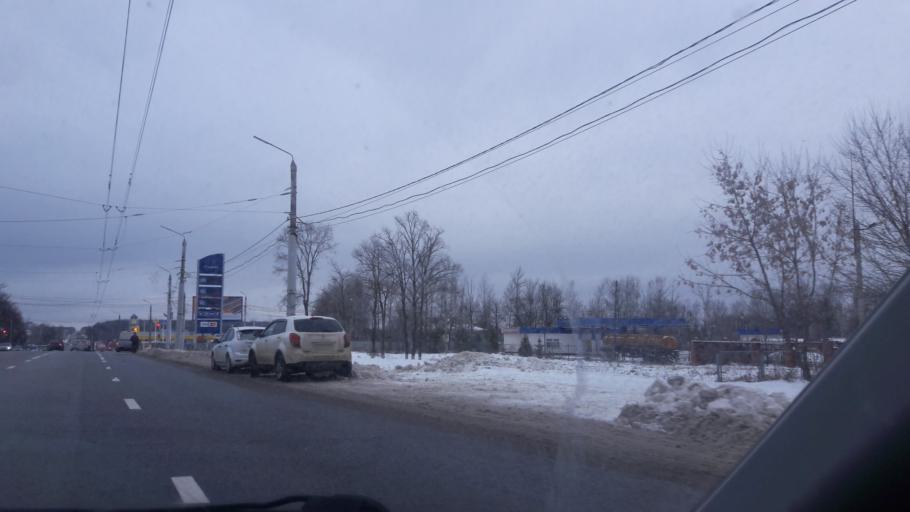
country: RU
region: Tula
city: Gorelki
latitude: 54.2402
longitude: 37.6193
